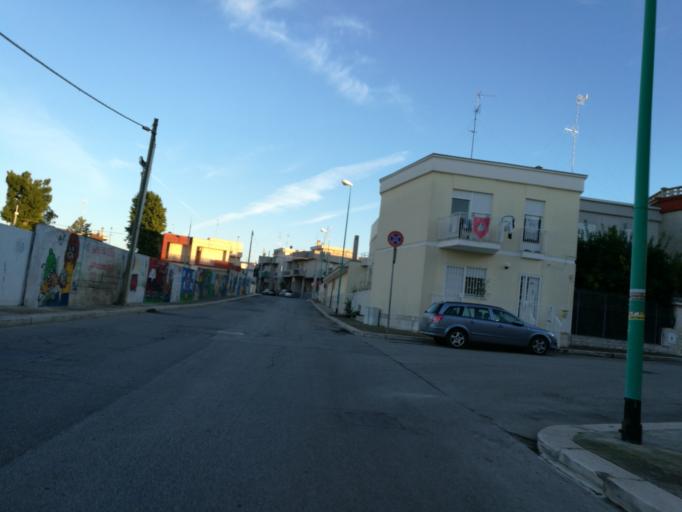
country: IT
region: Apulia
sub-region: Provincia di Bari
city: Adelfia
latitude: 41.0071
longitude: 16.8769
